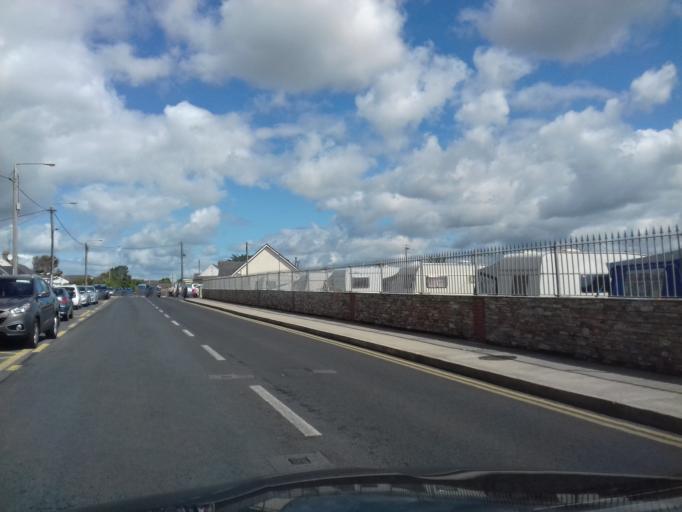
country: IE
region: Munster
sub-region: Waterford
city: Tra Mhor
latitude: 52.1611
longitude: -7.1402
